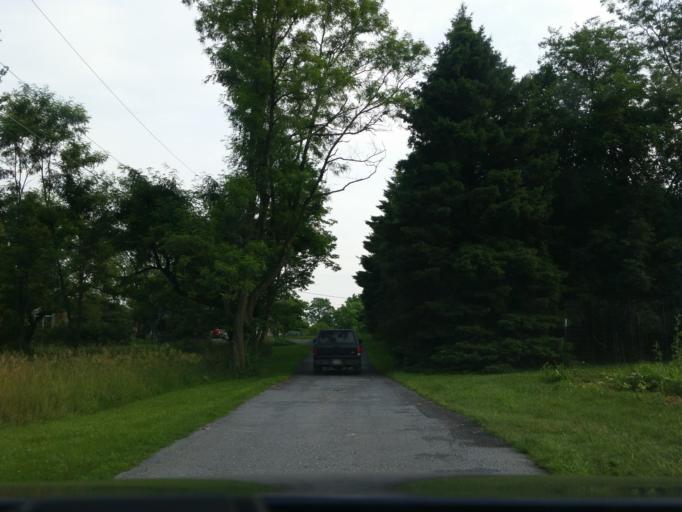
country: US
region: Pennsylvania
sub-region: Lebanon County
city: Jonestown
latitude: 40.4144
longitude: -76.5039
